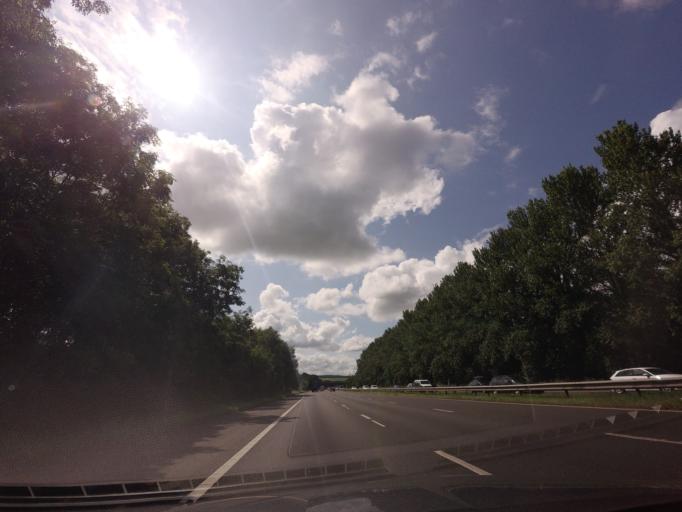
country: GB
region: England
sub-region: Lancashire
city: Carnforth
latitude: 54.1530
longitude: -2.7382
